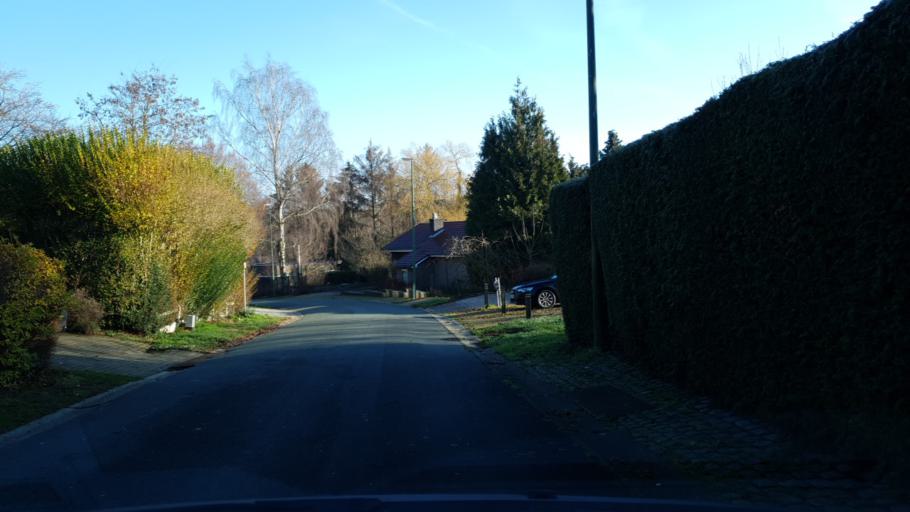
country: BE
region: Flanders
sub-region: Provincie Vlaams-Brabant
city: Herent
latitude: 50.8830
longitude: 4.6688
